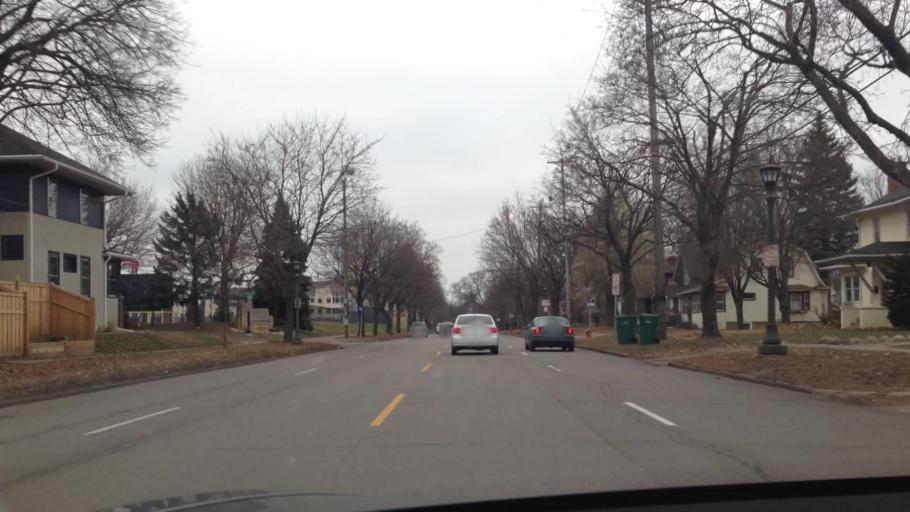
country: US
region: Minnesota
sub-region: Ramsey County
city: Falcon Heights
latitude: 44.9468
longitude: -93.1924
